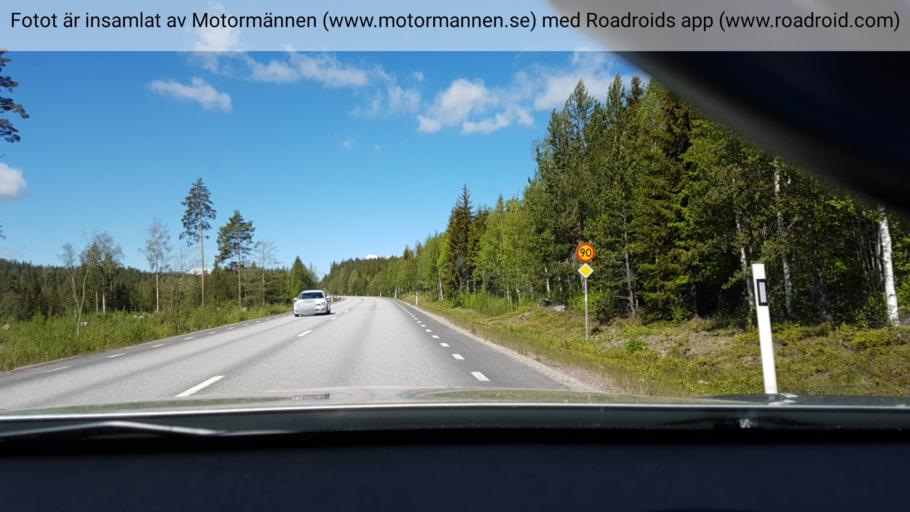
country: SE
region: Dalarna
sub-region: Faluns Kommun
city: Bjursas
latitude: 60.7494
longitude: 15.3592
